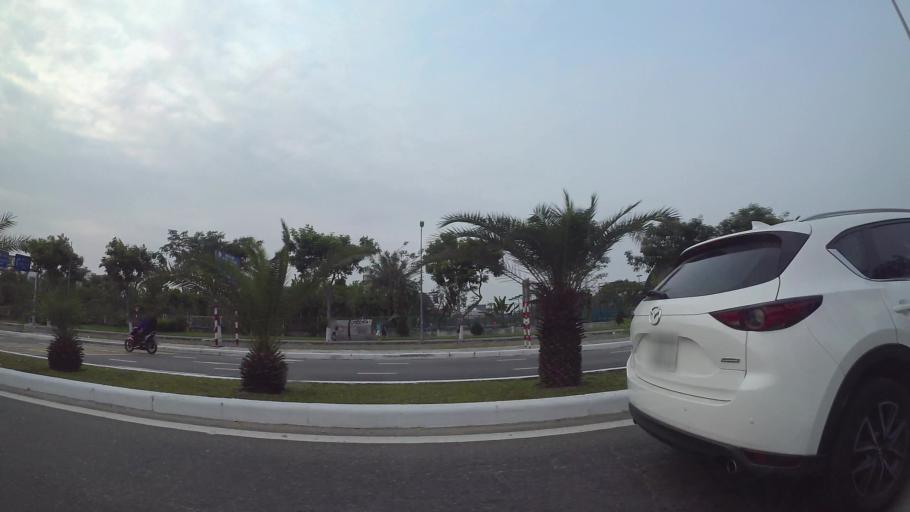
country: VN
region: Da Nang
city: Cam Le
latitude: 16.0332
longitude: 108.2256
